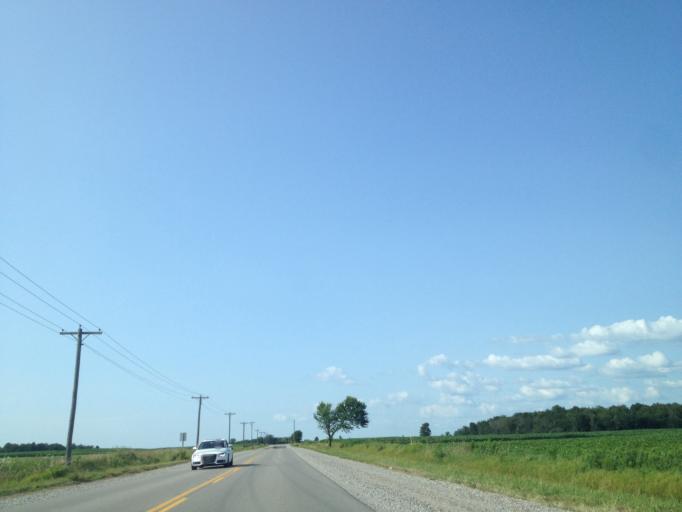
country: CA
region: Ontario
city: Aylmer
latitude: 42.8244
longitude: -80.8317
